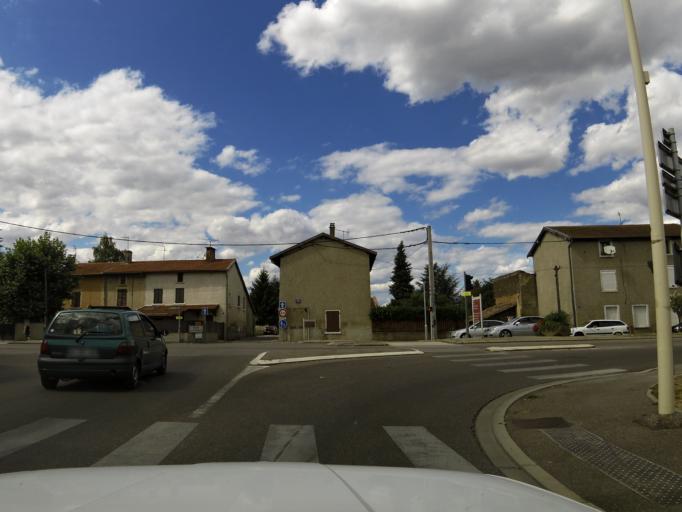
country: FR
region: Rhone-Alpes
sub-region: Departement de l'Isere
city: Pont-de-Cheruy
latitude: 45.7495
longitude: 5.1846
